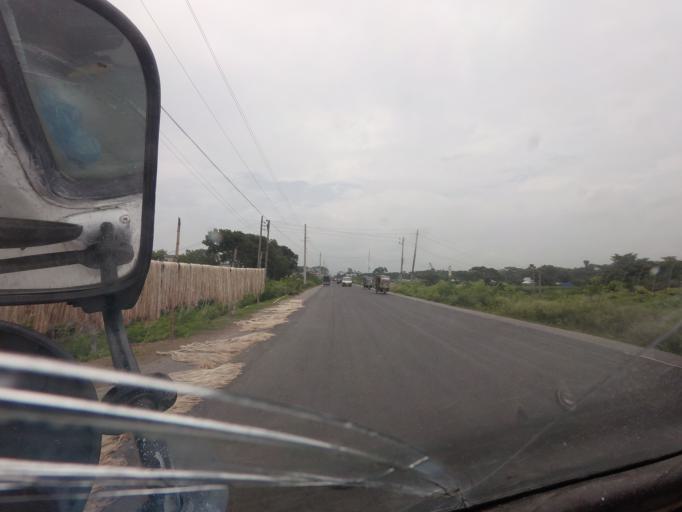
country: BD
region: Dhaka
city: Char Bhadrasan
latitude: 23.3878
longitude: 89.9895
